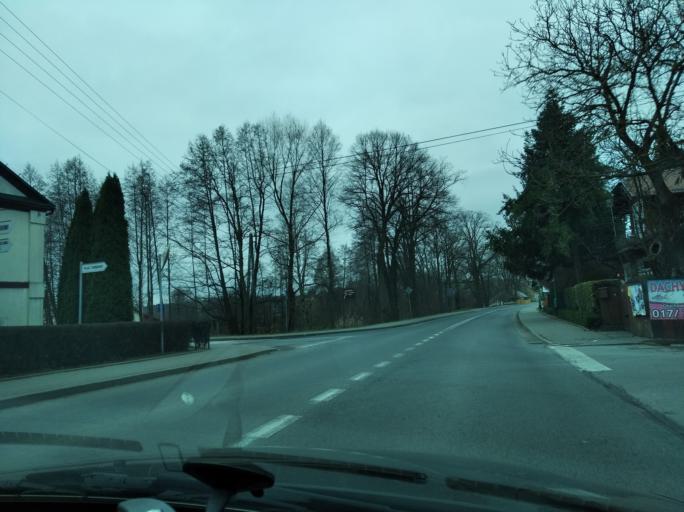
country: PL
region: Subcarpathian Voivodeship
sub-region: Powiat lancucki
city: Zolynia
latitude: 50.1634
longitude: 22.3096
